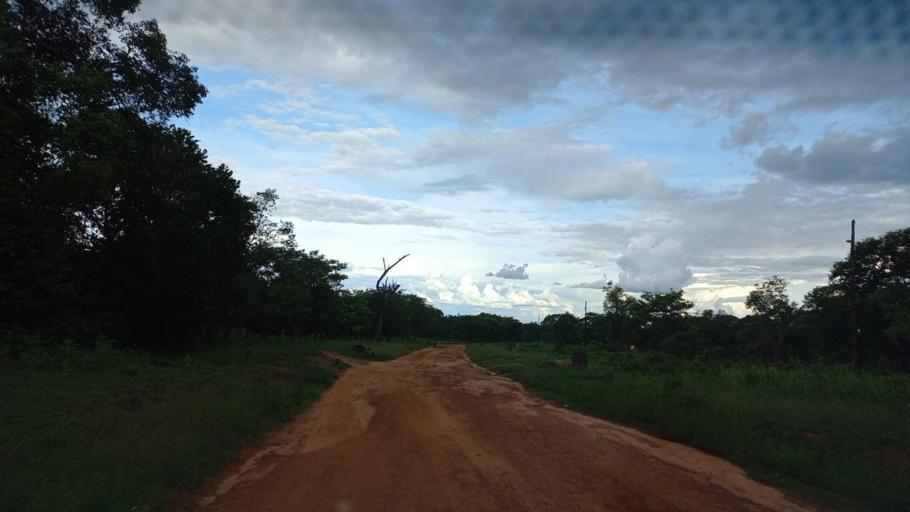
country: ZM
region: North-Western
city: Mwinilunga
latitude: -11.7738
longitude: 24.3929
